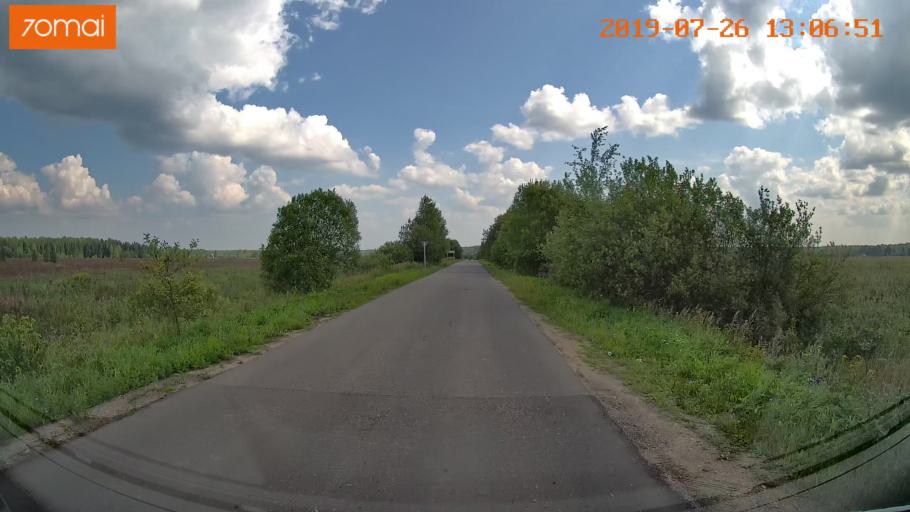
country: RU
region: Ivanovo
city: Bogorodskoye
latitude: 57.0681
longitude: 41.0515
